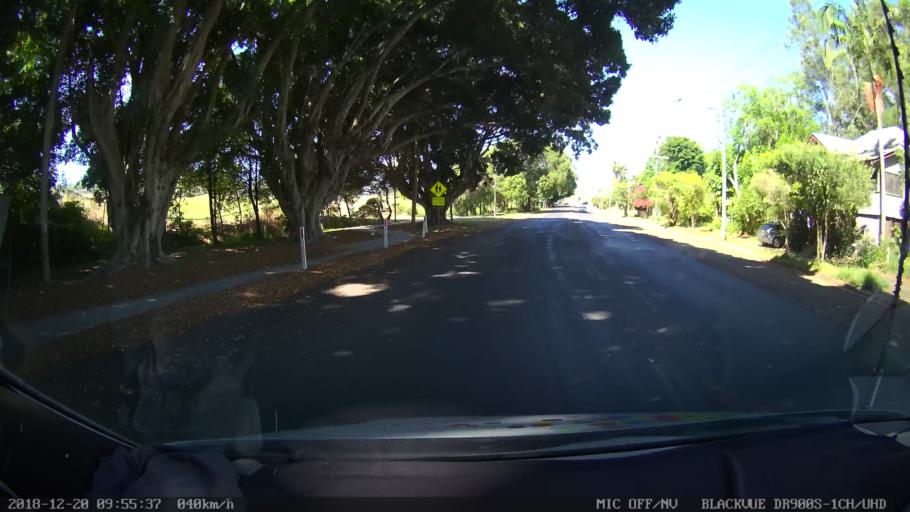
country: AU
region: New South Wales
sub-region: Lismore Municipality
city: Lismore
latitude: -28.8071
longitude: 153.2729
